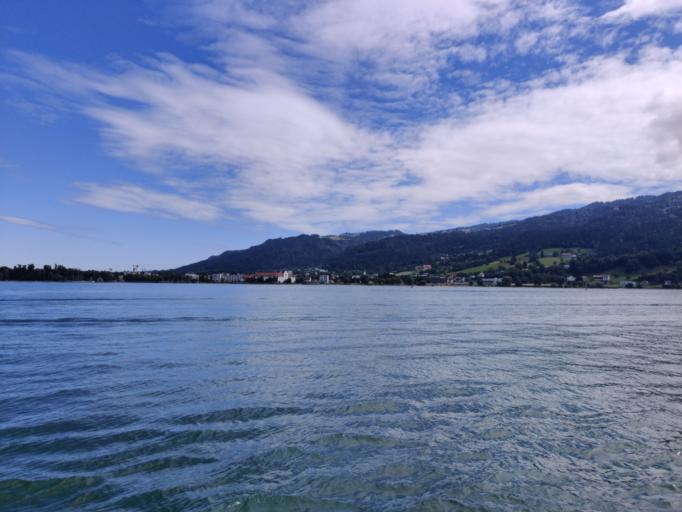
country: AT
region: Vorarlberg
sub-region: Politischer Bezirk Bregenz
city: Bregenz
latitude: 47.5193
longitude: 9.7351
